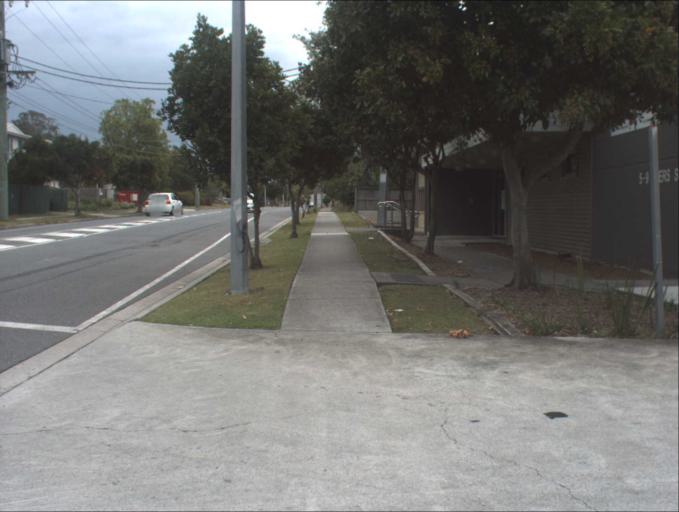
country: AU
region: Queensland
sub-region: Logan
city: Logan City
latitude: -27.6601
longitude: 153.1168
